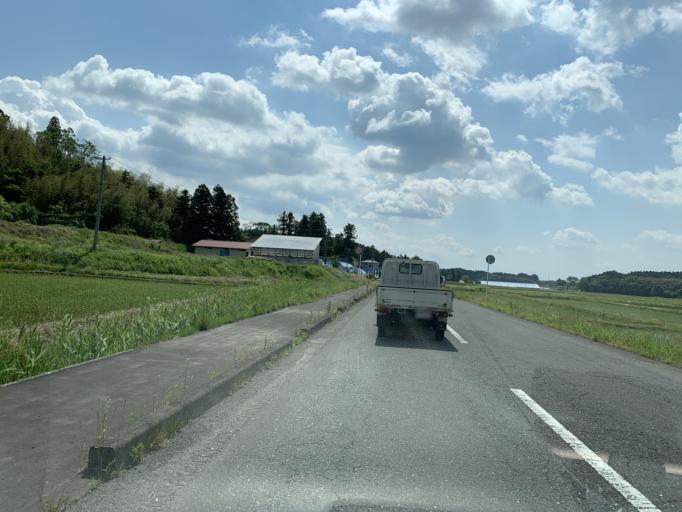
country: JP
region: Miyagi
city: Furukawa
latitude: 38.6893
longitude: 140.9479
